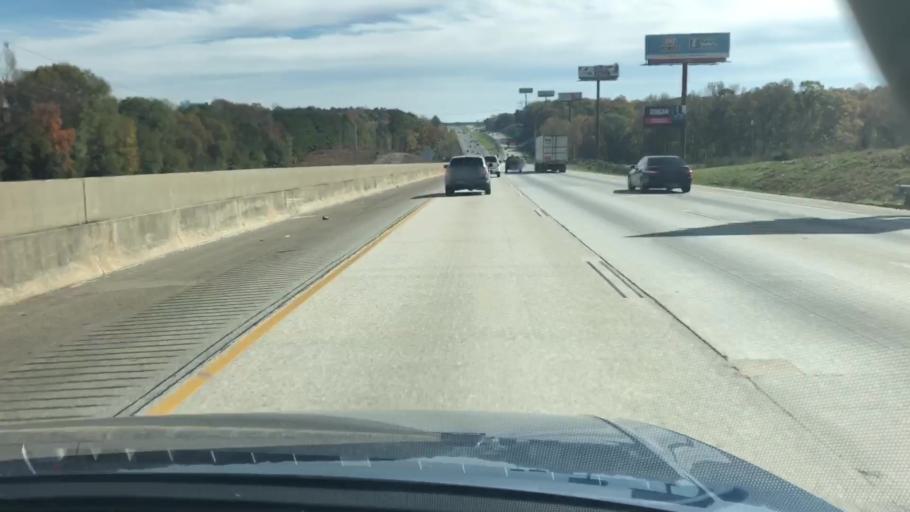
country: US
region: Georgia
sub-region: Monroe County
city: Forsyth
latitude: 33.0010
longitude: -83.8618
